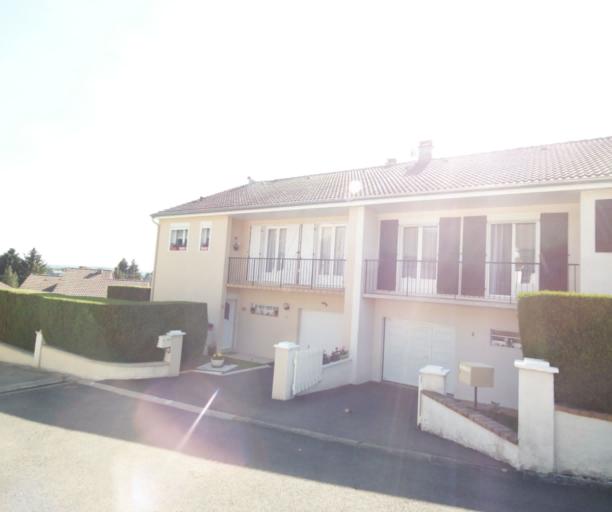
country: FR
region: Champagne-Ardenne
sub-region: Departement des Ardennes
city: Warcq
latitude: 49.7853
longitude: 4.6996
